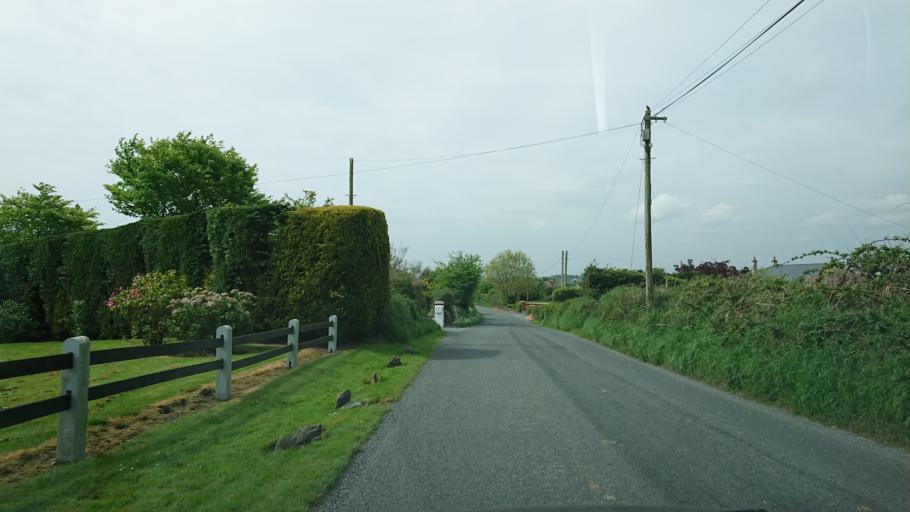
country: IE
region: Munster
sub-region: Waterford
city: Waterford
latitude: 52.2159
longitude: -7.0761
